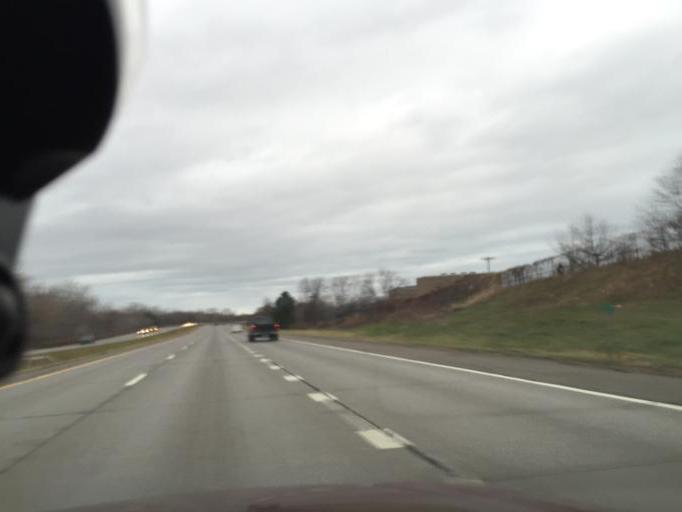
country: US
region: New York
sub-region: Monroe County
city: Greece
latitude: 43.2200
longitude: -77.6746
